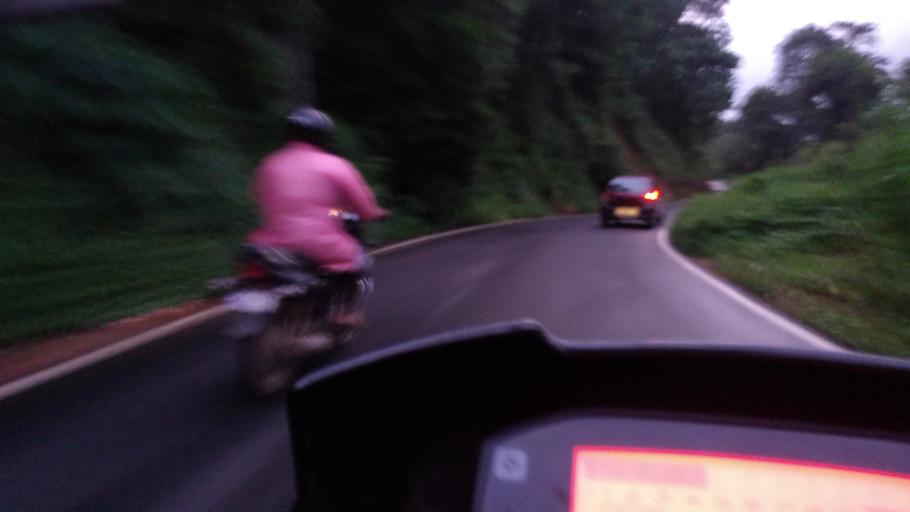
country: IN
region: Kerala
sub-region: Idukki
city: Munnar
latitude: 9.9614
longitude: 77.0707
